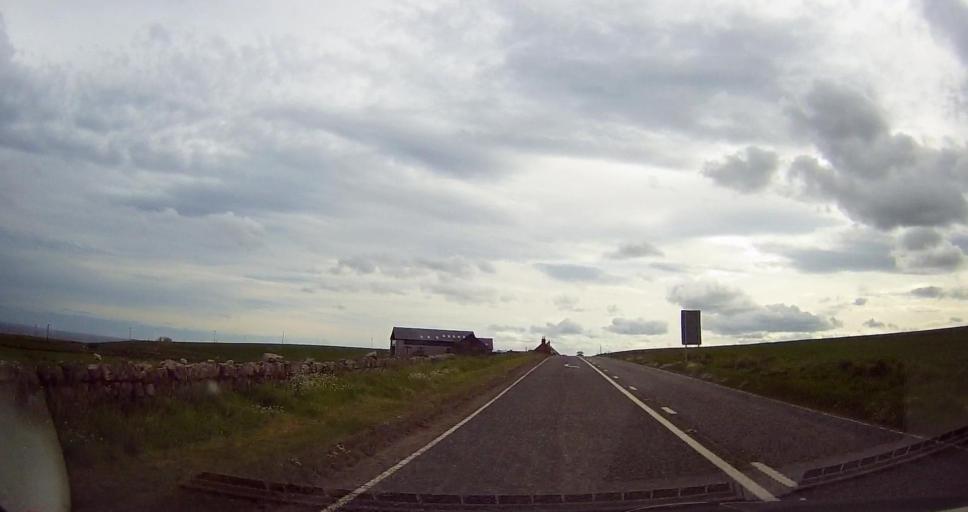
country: GB
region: Scotland
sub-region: Aberdeenshire
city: Stonehaven
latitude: 56.9184
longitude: -2.2114
